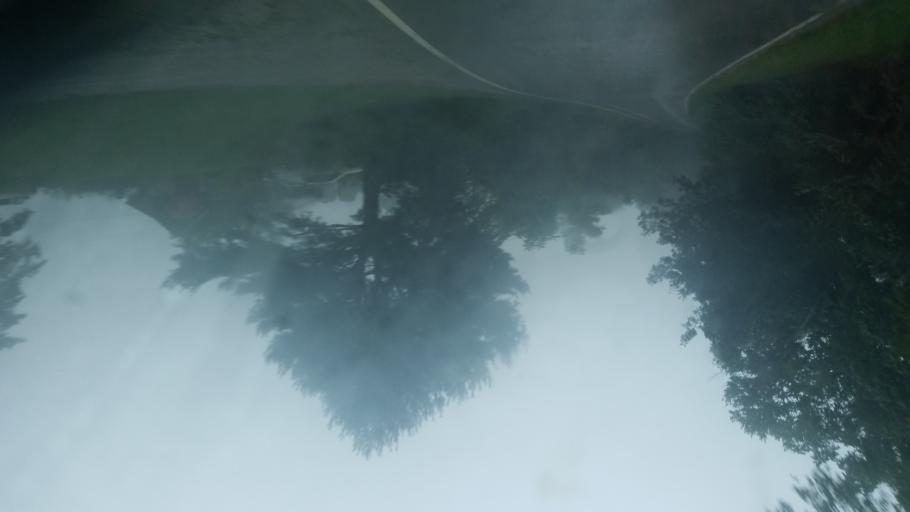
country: US
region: Kentucky
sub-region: Fleming County
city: Flemingsburg
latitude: 38.4752
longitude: -83.5124
